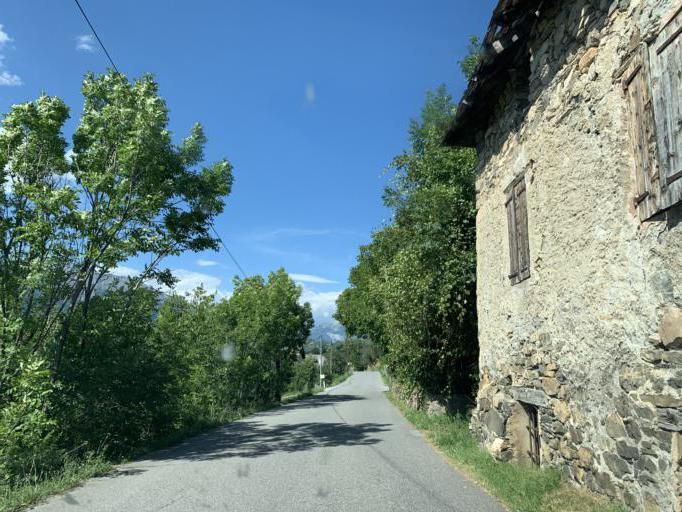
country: FR
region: Provence-Alpes-Cote d'Azur
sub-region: Departement des Hautes-Alpes
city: Embrun
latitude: 44.5830
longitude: 6.5289
